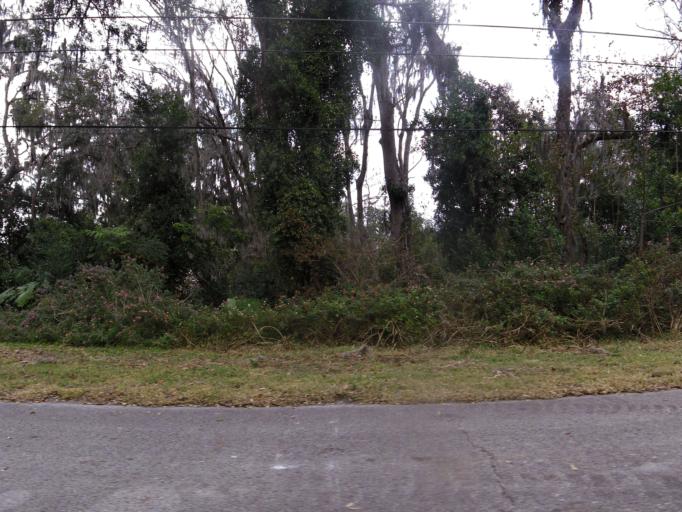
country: US
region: Florida
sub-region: Duval County
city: Jacksonville
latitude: 30.2433
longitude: -81.6304
